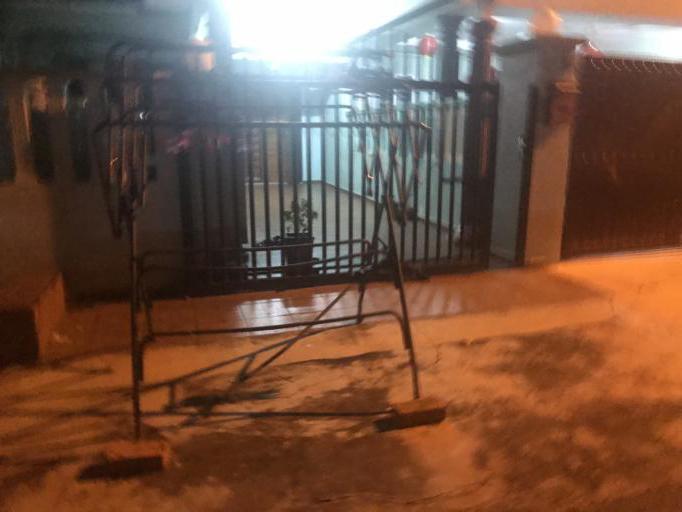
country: MY
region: Selangor
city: Klang
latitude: 3.0100
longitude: 101.4281
